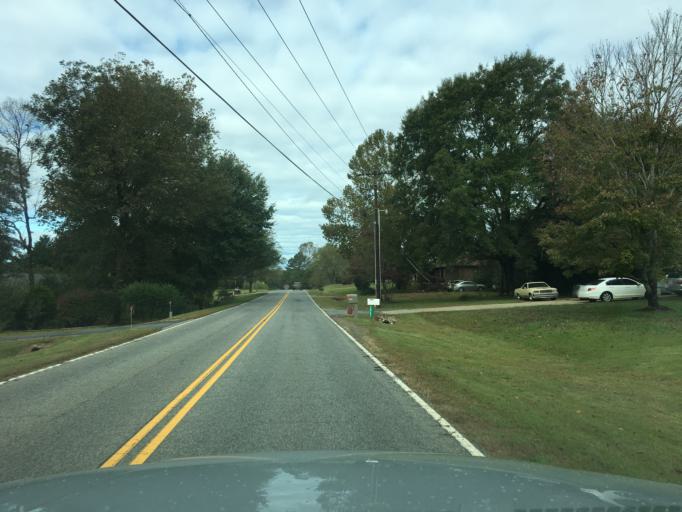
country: US
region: South Carolina
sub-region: Greenville County
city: Greer
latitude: 34.9768
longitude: -82.2088
